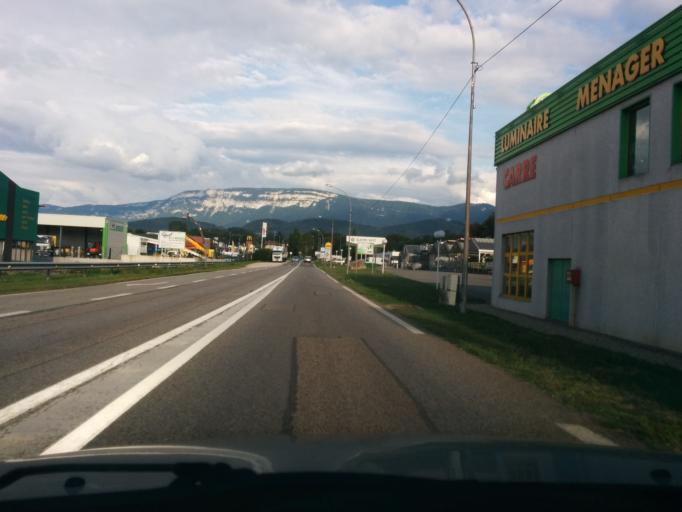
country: FR
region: Rhone-Alpes
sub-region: Departement de la Savoie
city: Le Pont-de-Beauvoisin
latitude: 45.5293
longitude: 5.6854
